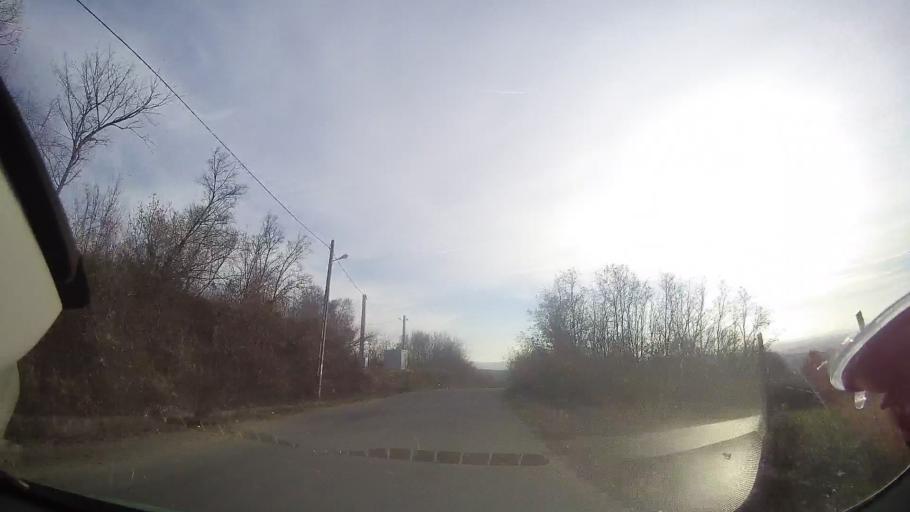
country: RO
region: Bihor
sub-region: Comuna Sarbi
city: Burzuc
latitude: 47.1171
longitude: 22.1791
